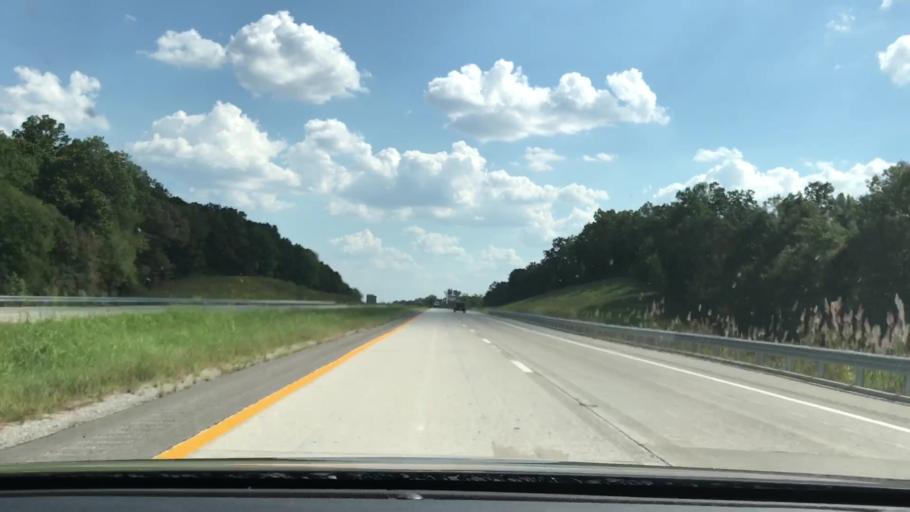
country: US
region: Kentucky
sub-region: Ohio County
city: Oak Grove
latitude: 37.3741
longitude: -86.8031
